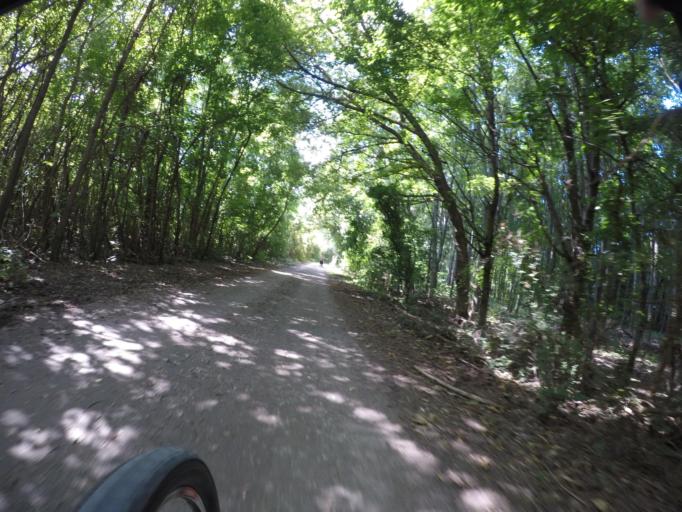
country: AT
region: Lower Austria
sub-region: Politischer Bezirk Ganserndorf
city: Gross-Enzersdorf
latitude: 48.1810
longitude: 16.5231
